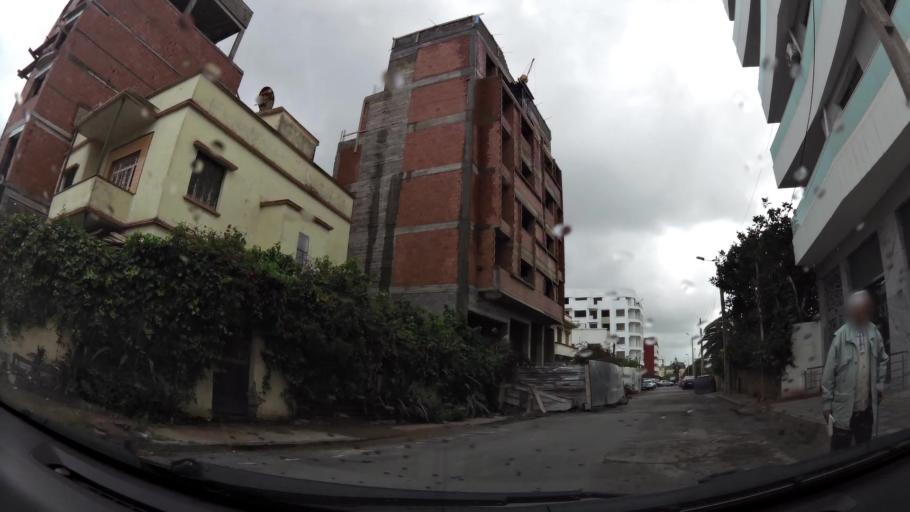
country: MA
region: Grand Casablanca
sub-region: Casablanca
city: Casablanca
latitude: 33.5714
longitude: -7.6192
